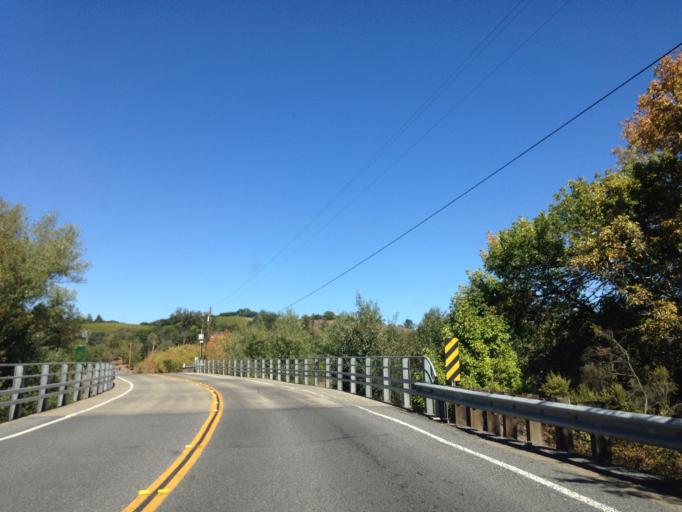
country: US
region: California
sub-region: Sonoma County
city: Forestville
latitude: 38.4935
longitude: -122.8528
